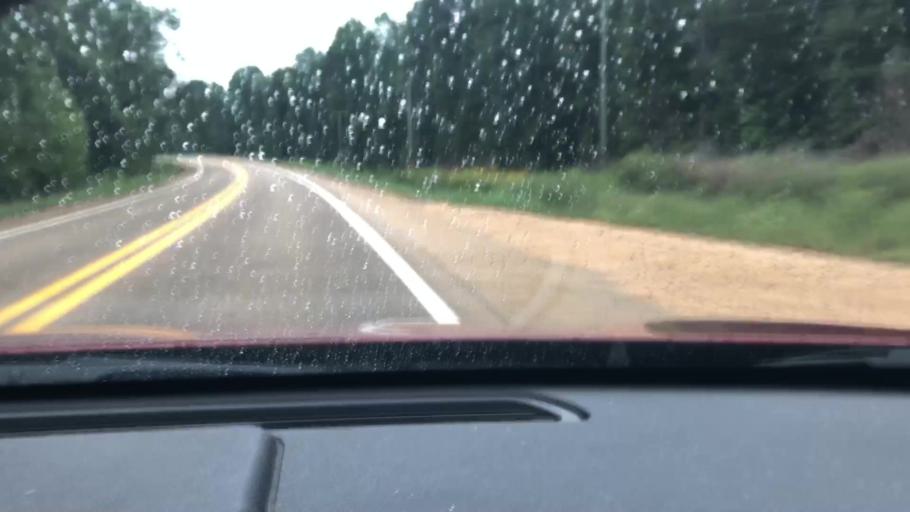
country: US
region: Arkansas
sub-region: Lafayette County
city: Stamps
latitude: 33.3579
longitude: -93.4060
